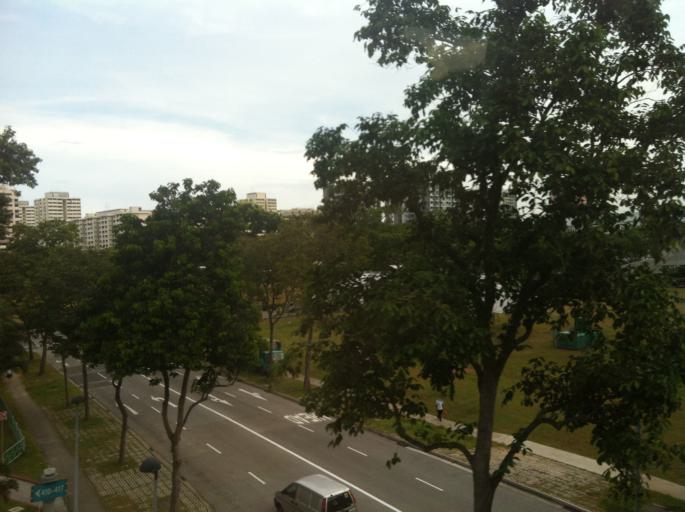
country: SG
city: Singapore
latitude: 1.3187
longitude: 103.8978
